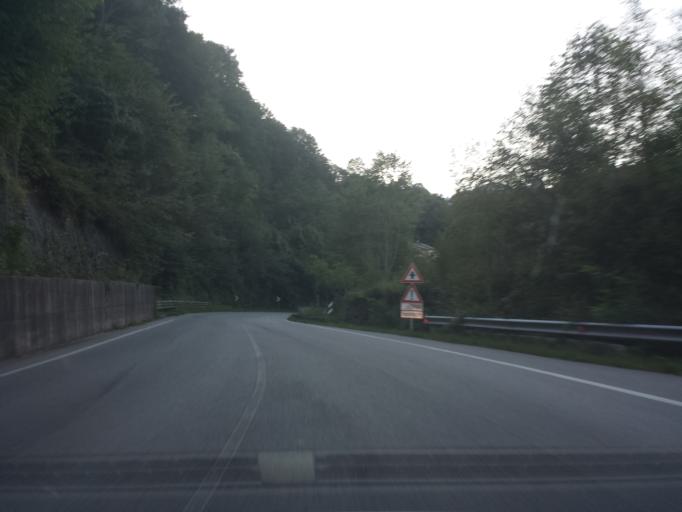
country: IT
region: Veneto
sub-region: Provincia di Vicenza
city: Recoaro Terme
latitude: 45.7031
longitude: 11.2436
